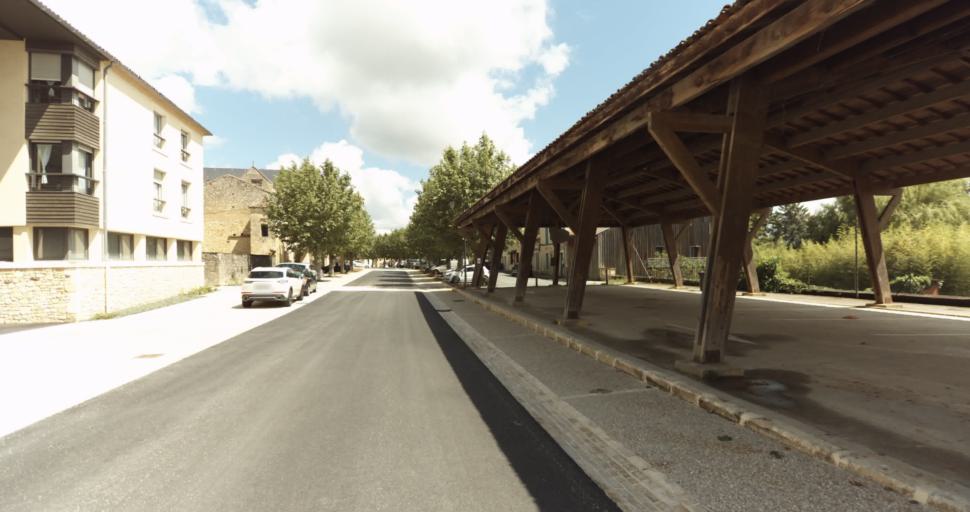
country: FR
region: Aquitaine
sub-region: Departement de la Dordogne
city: Beaumont-du-Perigord
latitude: 44.7679
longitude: 0.7685
